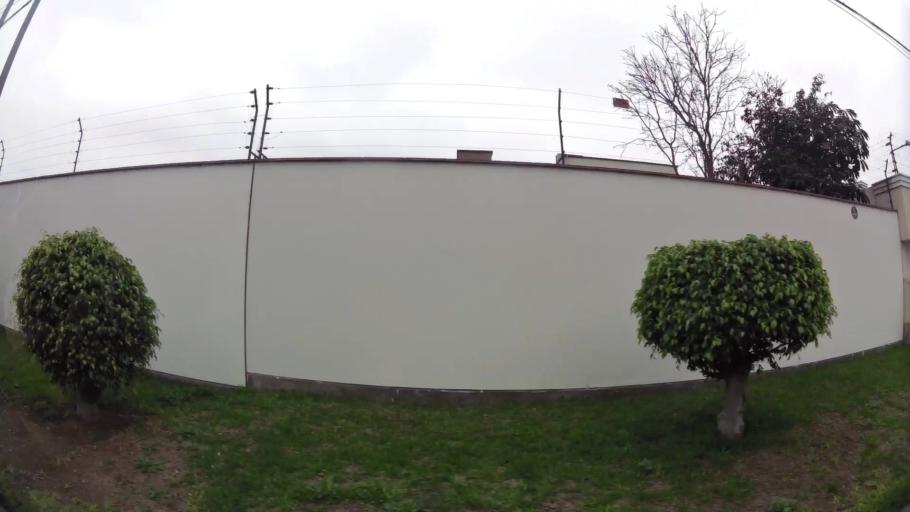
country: PE
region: Lima
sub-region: Lima
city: La Molina
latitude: -12.0863
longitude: -76.9216
